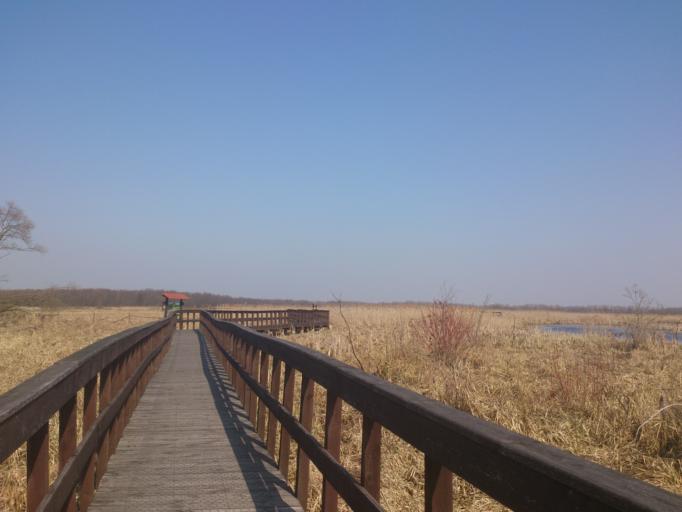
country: PL
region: Podlasie
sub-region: Powiat bialostocki
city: Tykocin
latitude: 53.1058
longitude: 22.7983
